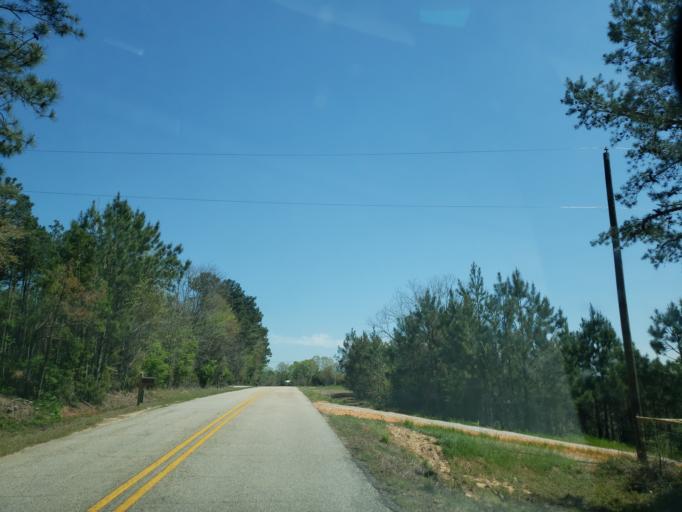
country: US
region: Alabama
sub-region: Tallapoosa County
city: Camp Hill
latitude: 32.6789
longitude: -85.6934
